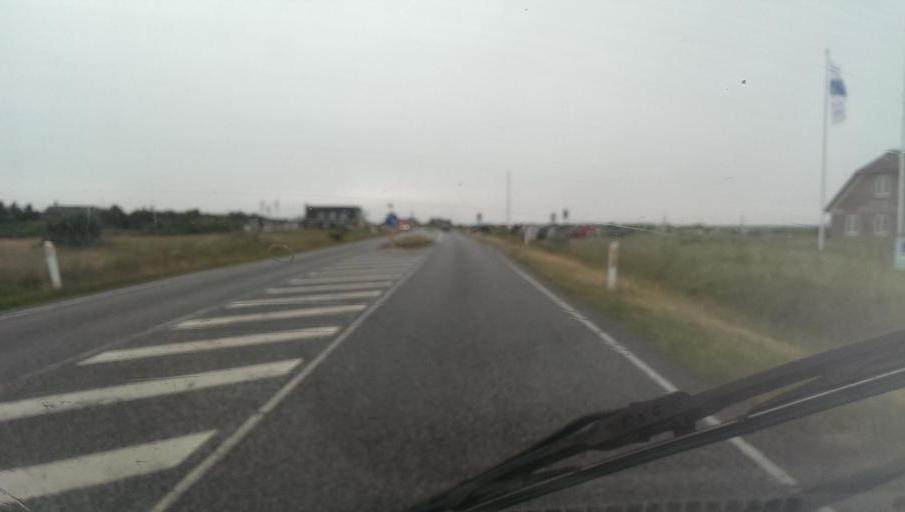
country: DK
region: Central Jutland
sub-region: Ringkobing-Skjern Kommune
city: Hvide Sande
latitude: 55.8619
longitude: 8.1809
